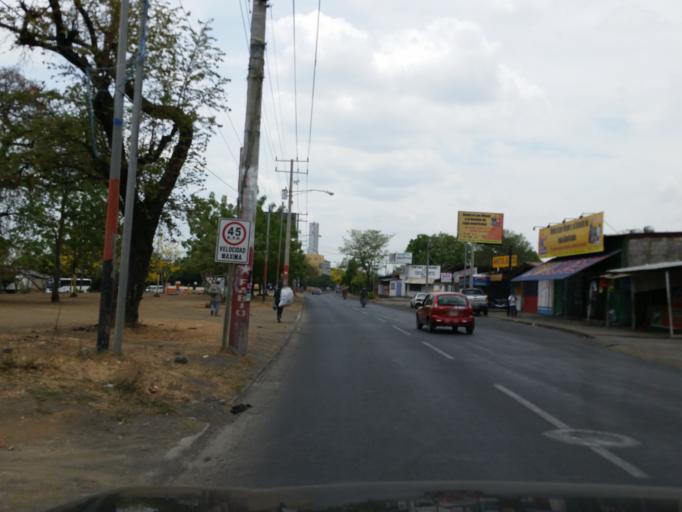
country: NI
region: Managua
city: Managua
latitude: 12.1536
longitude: -86.2638
